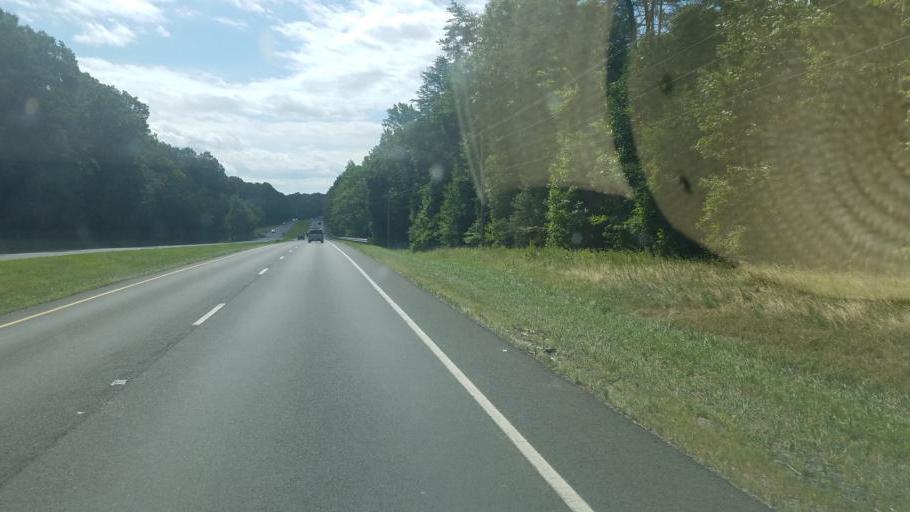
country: US
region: Virginia
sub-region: Fauquier County
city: Bealeton
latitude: 38.4639
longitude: -77.6728
